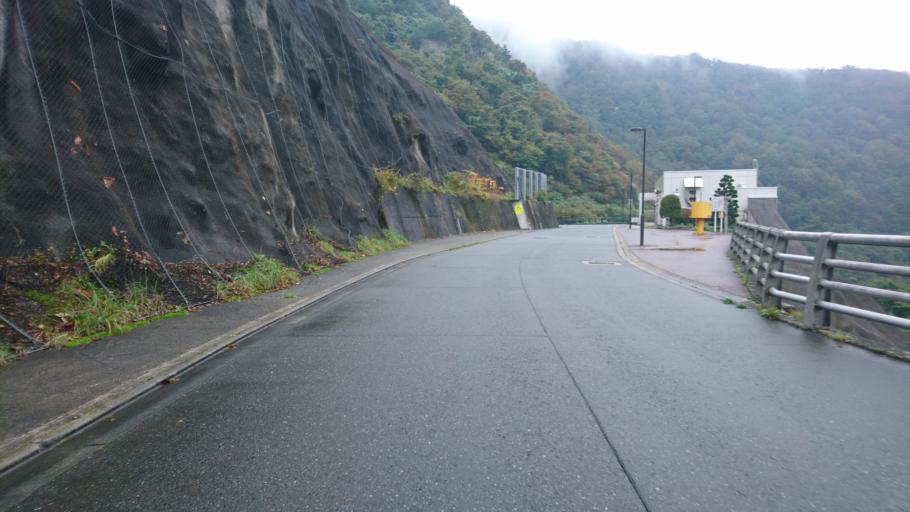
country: JP
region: Iwate
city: Kitakami
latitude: 39.3022
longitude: 140.8833
